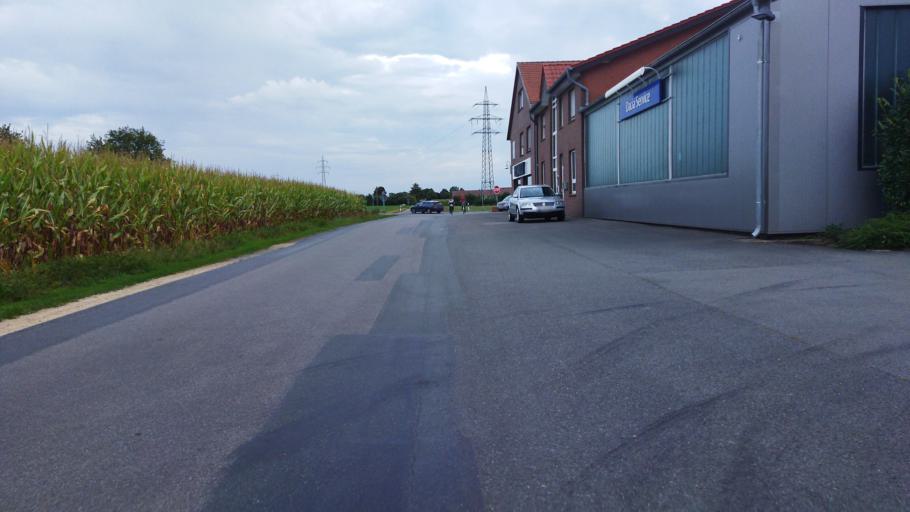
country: DE
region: Lower Saxony
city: Bad Laer
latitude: 52.0948
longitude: 8.0840
